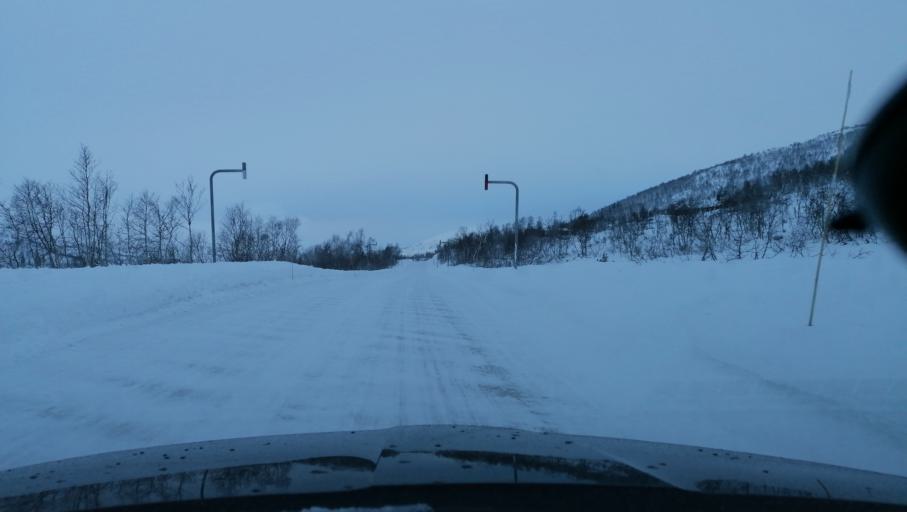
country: NO
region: Aust-Agder
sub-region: Bykle
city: Hovden
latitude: 59.6337
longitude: 7.4536
